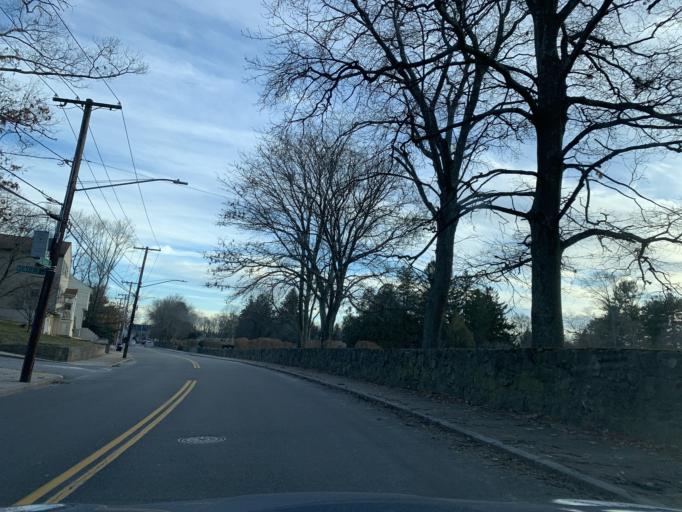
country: US
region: Massachusetts
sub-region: Norfolk County
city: Dedham
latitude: 42.2944
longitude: -71.1713
